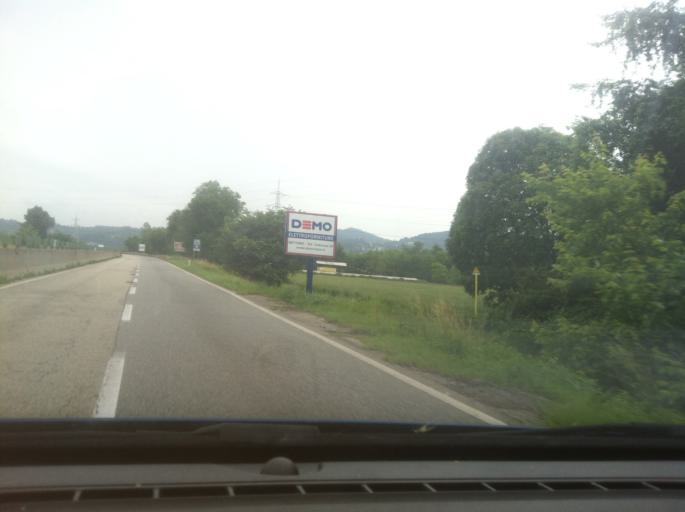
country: IT
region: Piedmont
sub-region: Provincia di Torino
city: San Mauro Torinese
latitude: 45.1126
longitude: 7.7432
